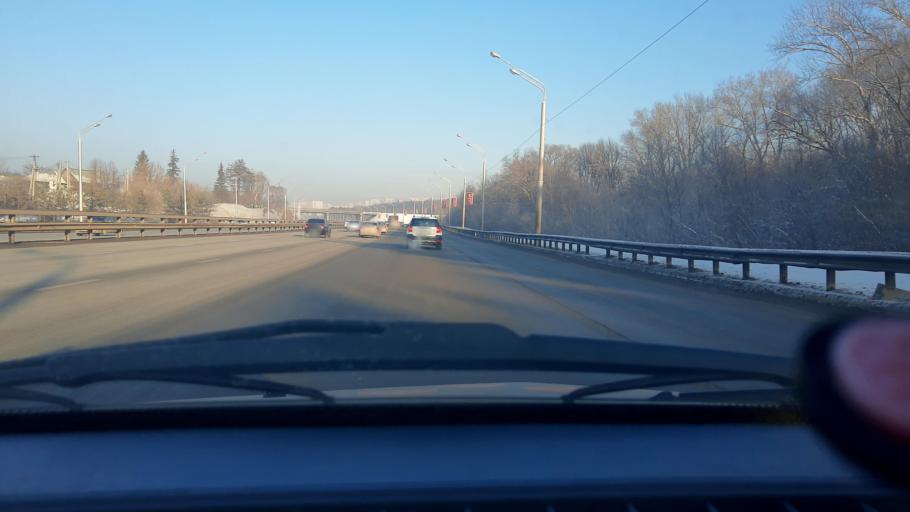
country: RU
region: Bashkortostan
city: Ufa
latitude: 54.7331
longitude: 56.0069
